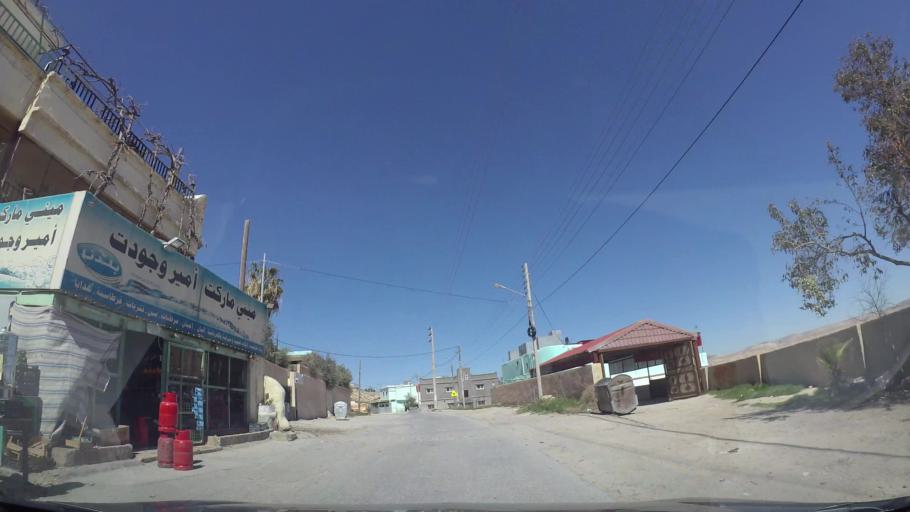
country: JO
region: Tafielah
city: At Tafilah
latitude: 30.8223
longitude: 35.5813
